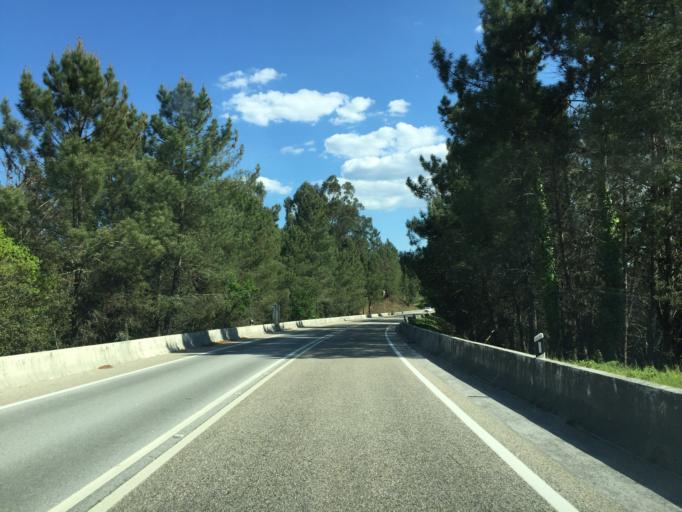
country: PT
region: Leiria
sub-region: Pedrogao Grande
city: Pedrogao Grande
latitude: 39.9201
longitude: -8.1544
